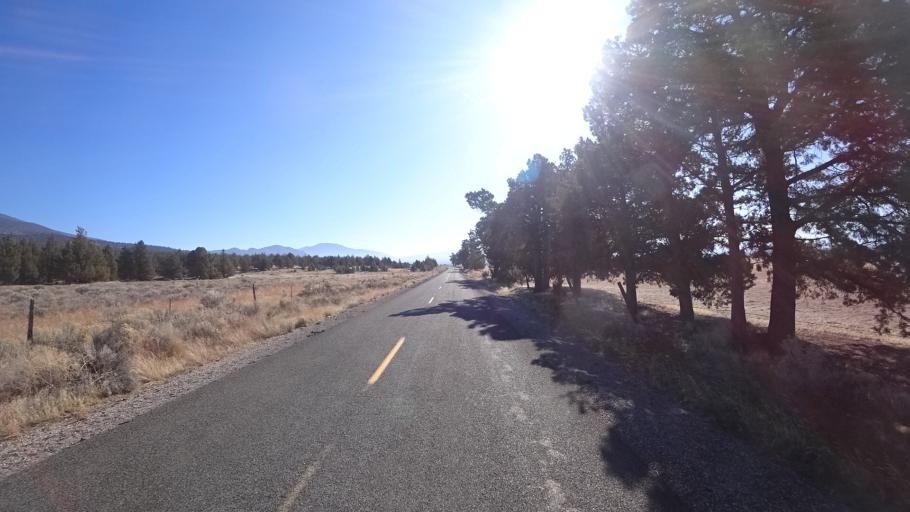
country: US
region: California
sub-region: Siskiyou County
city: Weed
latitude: 41.6160
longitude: -122.3184
